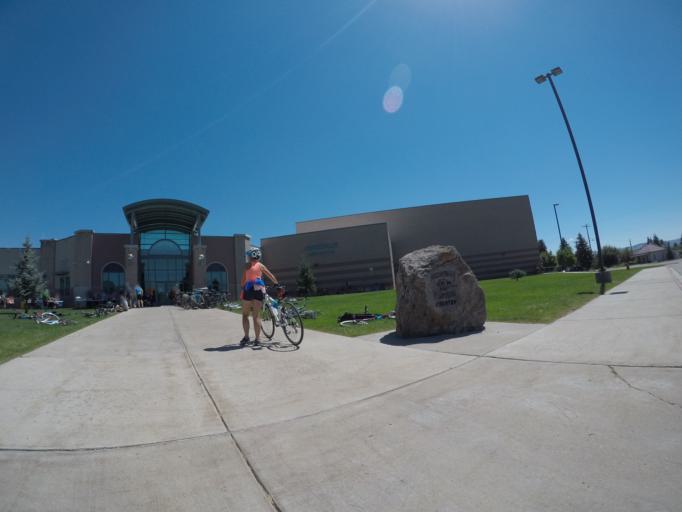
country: US
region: Idaho
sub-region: Bear Lake County
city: Montpelier
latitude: 42.0824
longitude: -110.9558
